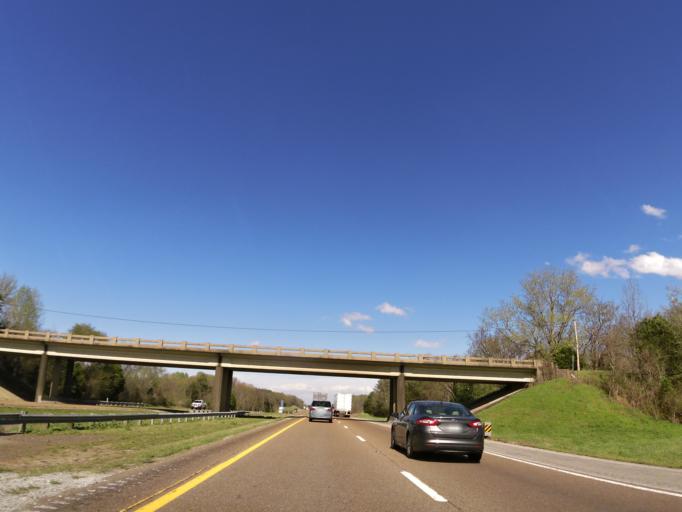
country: US
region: Tennessee
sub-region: Gibson County
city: Medina
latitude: 35.7365
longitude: -88.5845
